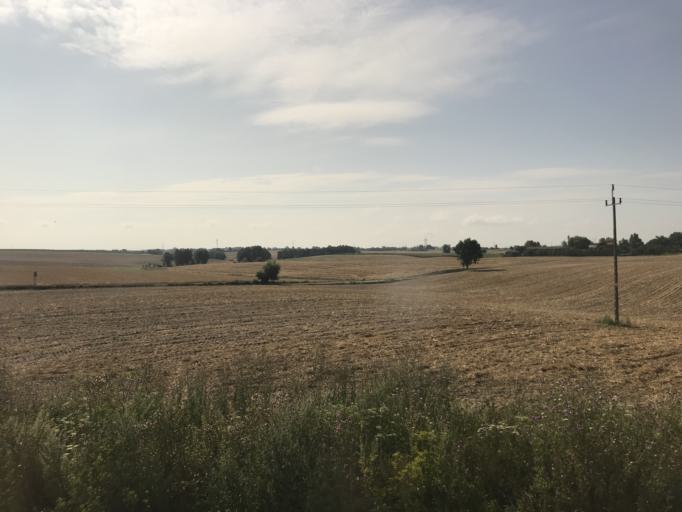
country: PL
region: Kujawsko-Pomorskie
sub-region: Powiat swiecki
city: Pruszcz
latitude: 53.3652
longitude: 18.2525
